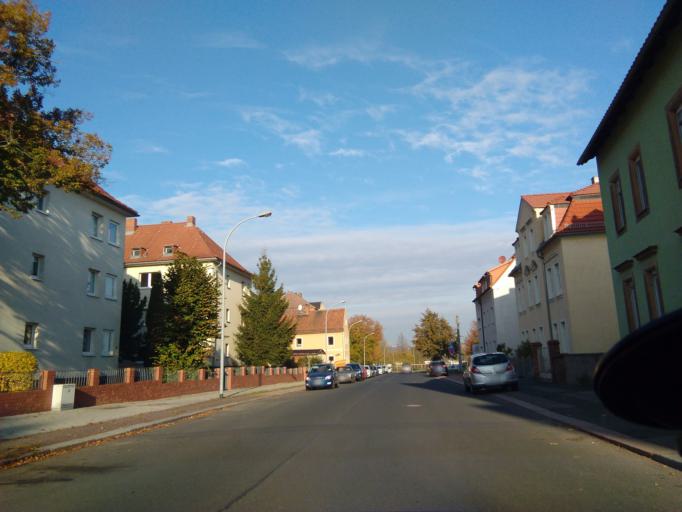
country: DE
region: Saxony
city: Meissen
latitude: 51.1568
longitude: 13.5065
